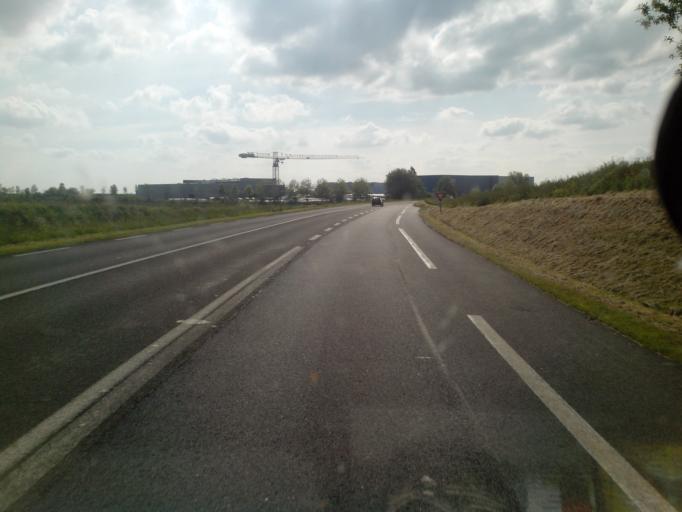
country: FR
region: Haute-Normandie
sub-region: Departement de la Seine-Maritime
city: Saint-Saens
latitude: 49.6545
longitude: 1.2681
